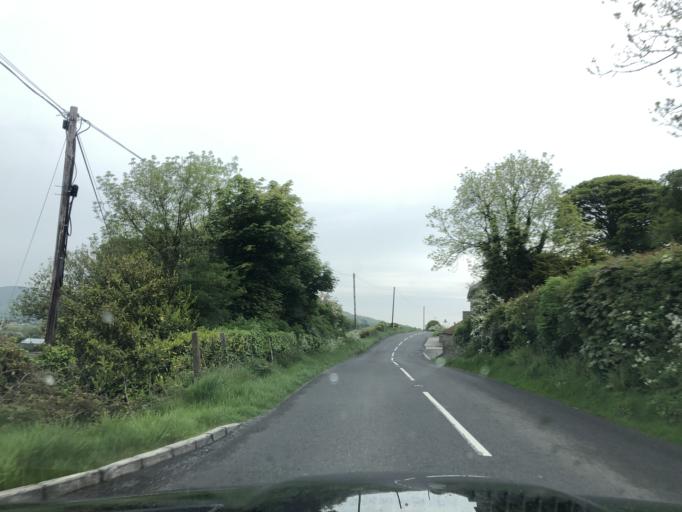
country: GB
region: Northern Ireland
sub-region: Down District
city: Castlewellan
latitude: 54.2203
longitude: -6.0191
